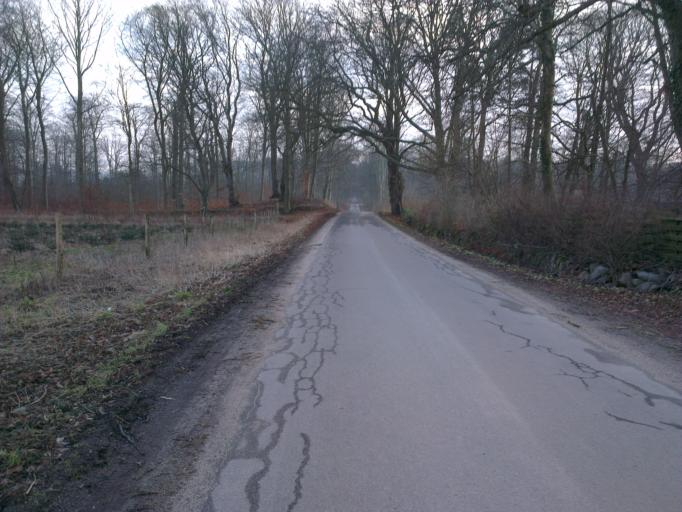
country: DK
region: Capital Region
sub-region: Frederikssund Kommune
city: Jaegerspris
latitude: 55.8702
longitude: 11.9860
